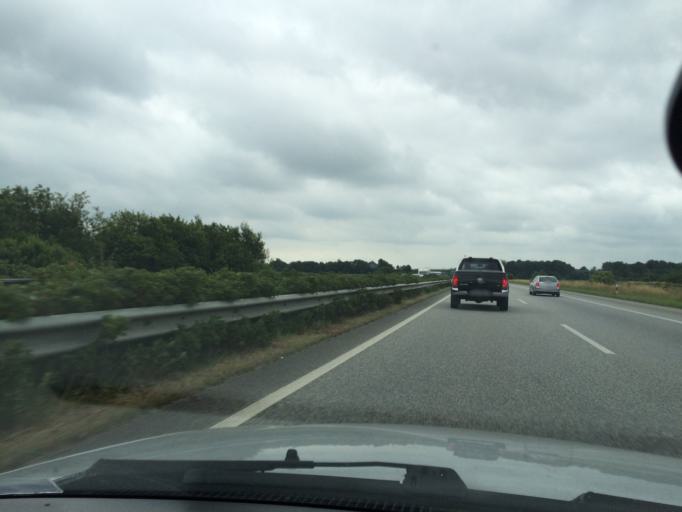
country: DE
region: Schleswig-Holstein
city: Sankelmark
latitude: 54.7072
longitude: 9.4010
